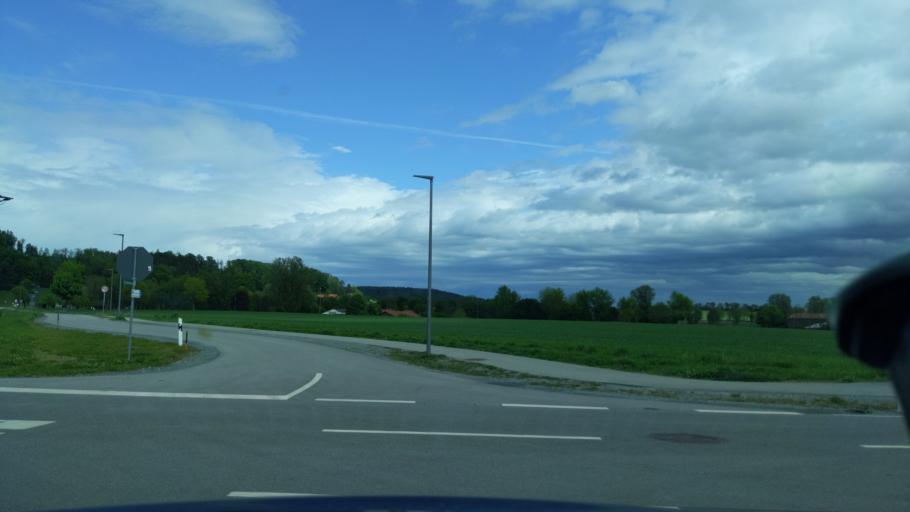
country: DE
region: Bavaria
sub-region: Upper Bavaria
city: Steinhoring
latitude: 48.0908
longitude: 12.0352
